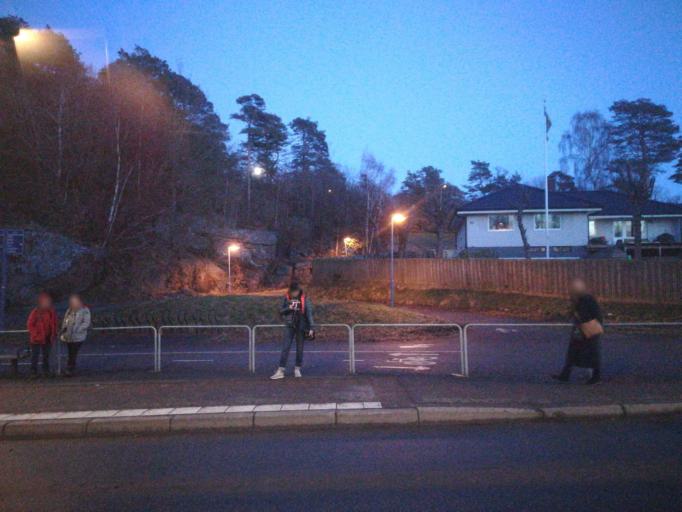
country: SE
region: Vaestra Goetaland
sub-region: Goteborg
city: Billdal
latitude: 57.6317
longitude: 11.9457
